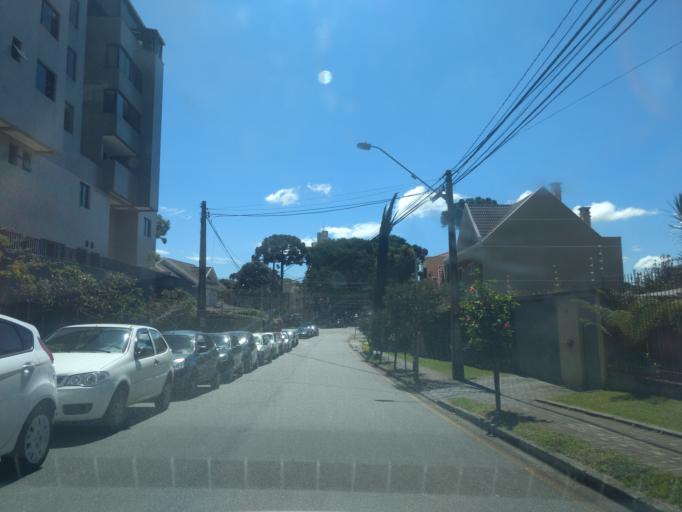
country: BR
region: Parana
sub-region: Curitiba
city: Curitiba
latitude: -25.4061
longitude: -49.2427
